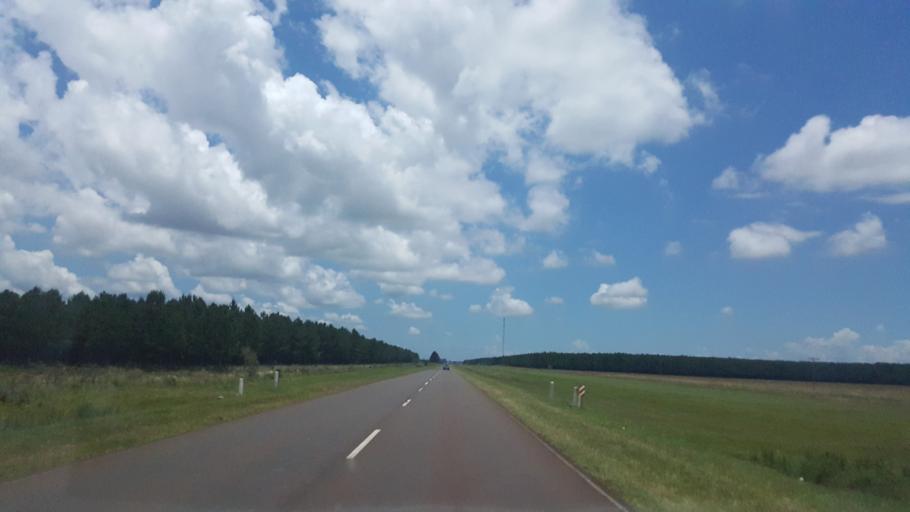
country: PY
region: Itapua
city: San Juan del Parana
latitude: -27.5150
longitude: -56.1456
